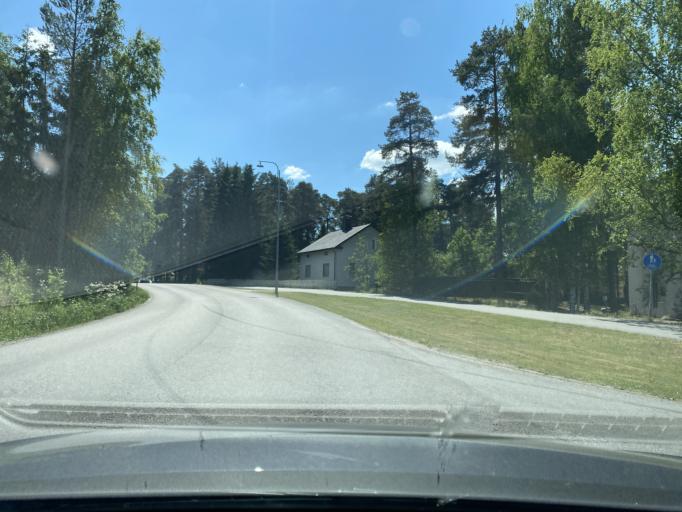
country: FI
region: Satakunta
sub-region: Rauma
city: Eura
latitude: 61.1214
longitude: 22.1589
